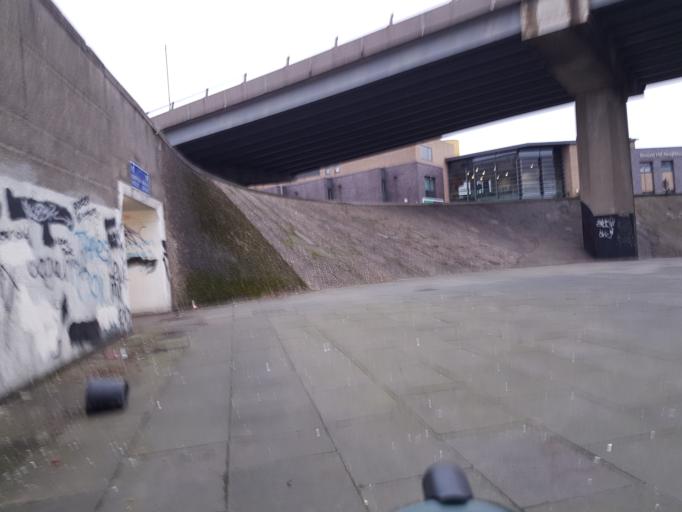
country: GB
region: England
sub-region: Liverpool
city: Liverpool
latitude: 53.4472
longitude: -2.9671
